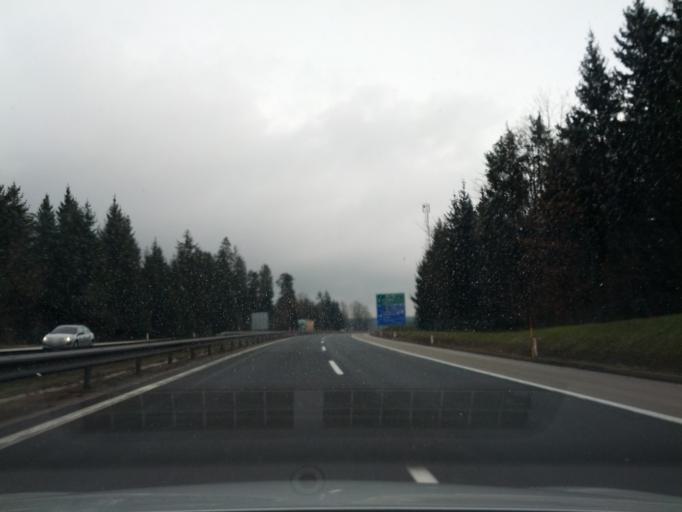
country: SI
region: Trzic
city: Bistrica pri Trzicu
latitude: 46.3132
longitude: 14.2696
